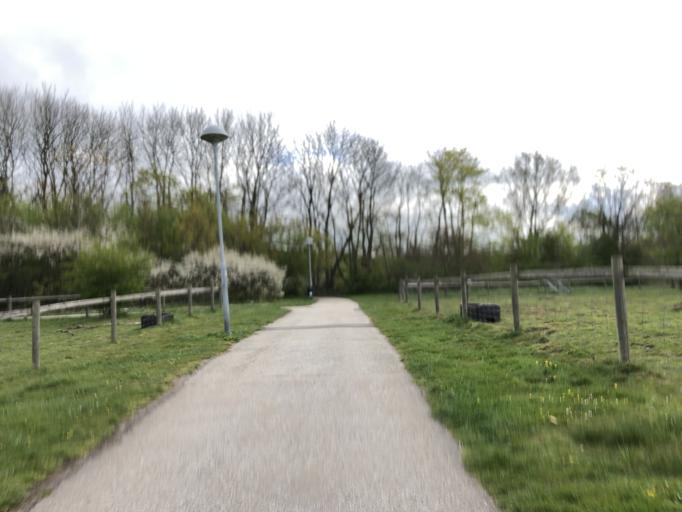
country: SE
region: Skane
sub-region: Lunds Kommun
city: Genarp
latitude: 55.6708
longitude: 13.3545
